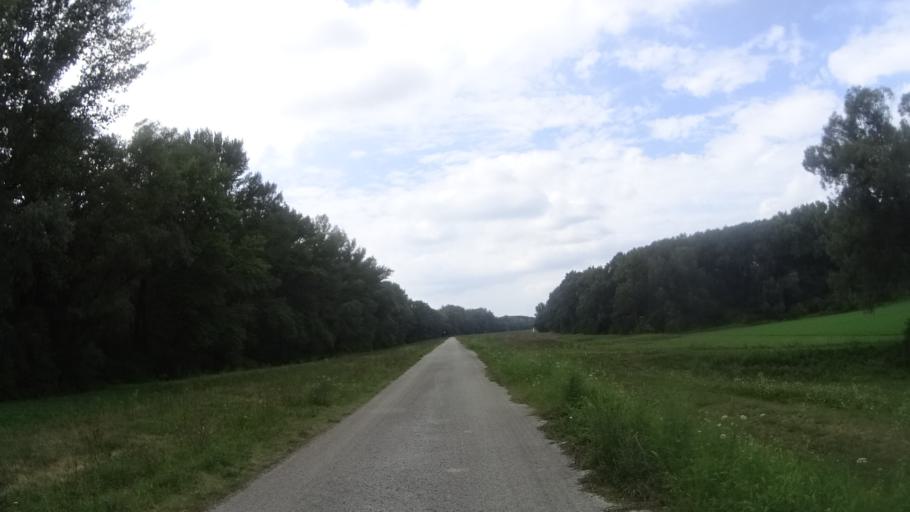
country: SK
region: Trnavsky
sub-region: Okres Dunajska Streda
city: Velky Meder
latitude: 47.7673
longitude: 17.7227
